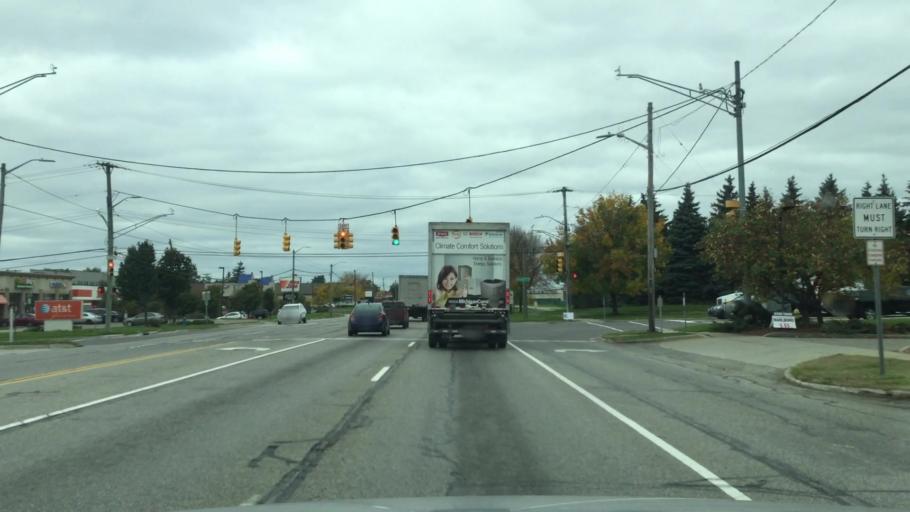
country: US
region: Michigan
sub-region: Oakland County
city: Waterford
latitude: 42.6600
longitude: -83.4053
